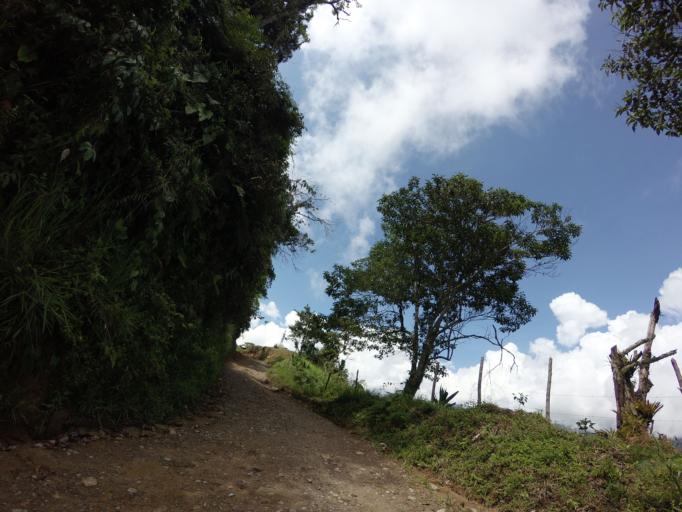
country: CO
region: Antioquia
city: Narino
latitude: 5.5137
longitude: -75.1722
